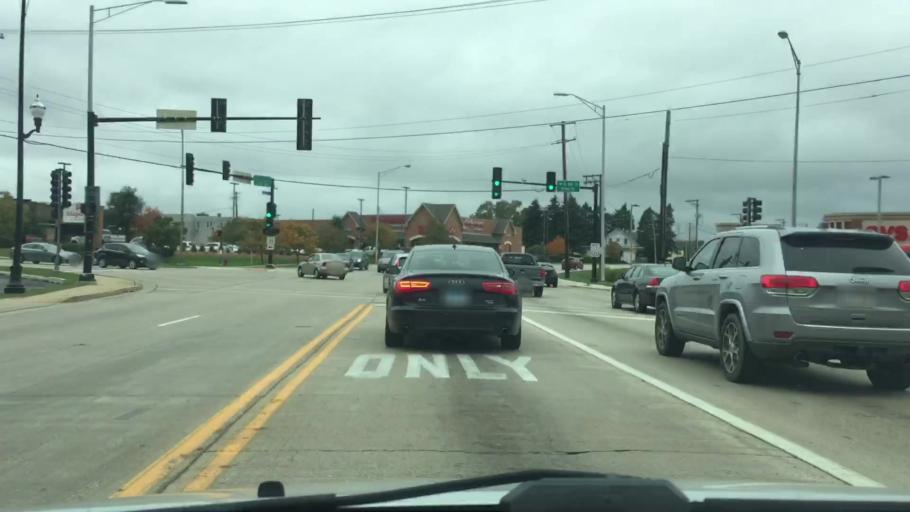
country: US
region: Illinois
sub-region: McHenry County
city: McHenry
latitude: 42.3447
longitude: -88.2729
